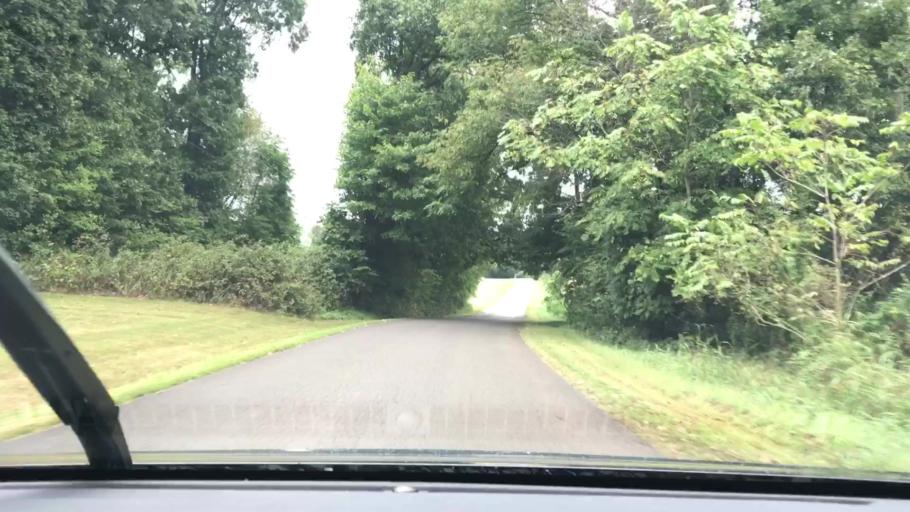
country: US
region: Kentucky
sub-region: Monroe County
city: Tompkinsville
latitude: 36.6252
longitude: -85.7719
